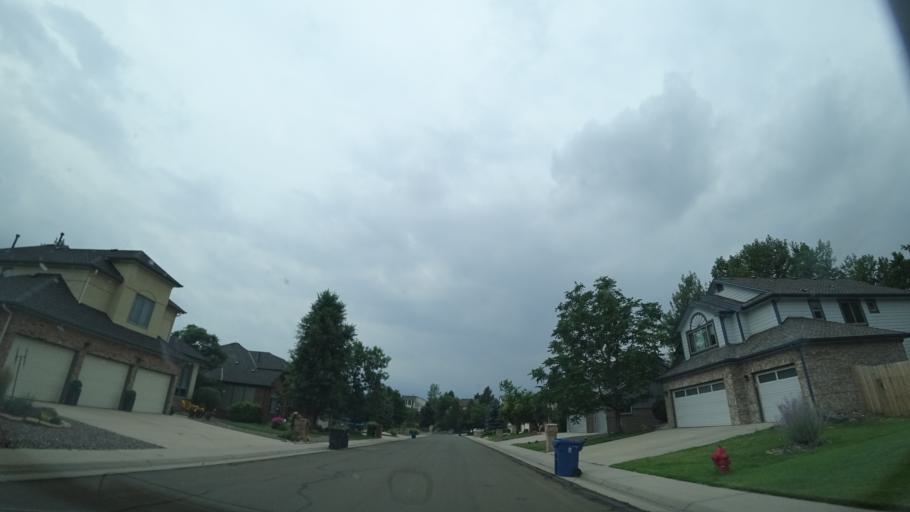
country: US
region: Colorado
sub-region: Jefferson County
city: West Pleasant View
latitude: 39.7098
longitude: -105.1450
